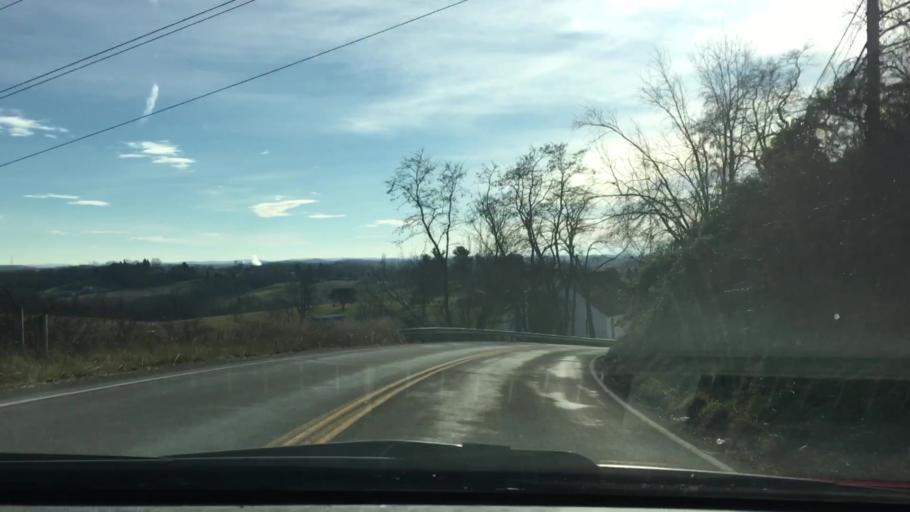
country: US
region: Pennsylvania
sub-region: Westmoreland County
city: West Newton
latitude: 40.2044
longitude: -79.7487
